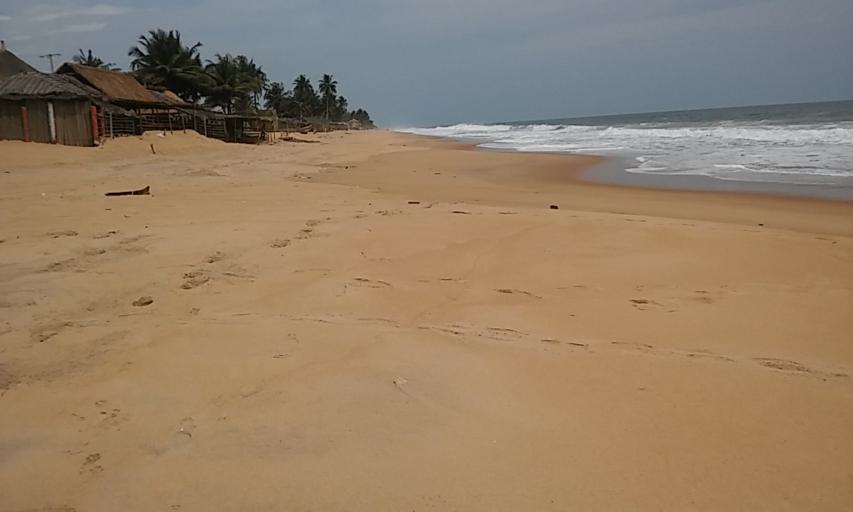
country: CI
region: Sud-Comoe
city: Grand-Bassam
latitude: 5.1974
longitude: -3.7544
